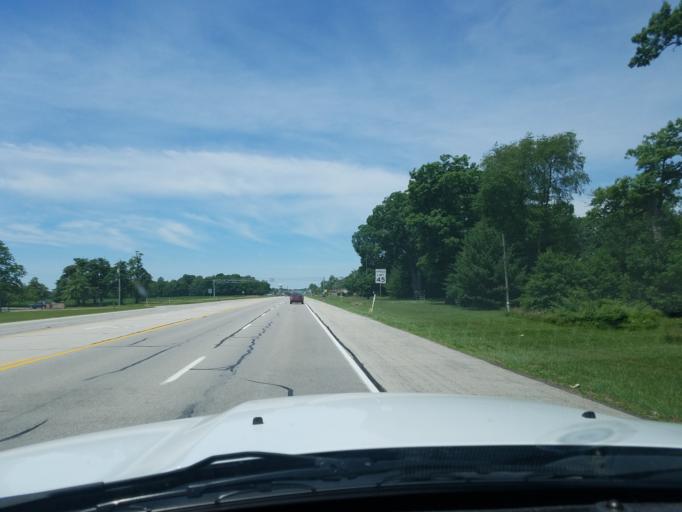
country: US
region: Indiana
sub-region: Delaware County
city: Daleville
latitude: 40.1135
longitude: -85.5453
